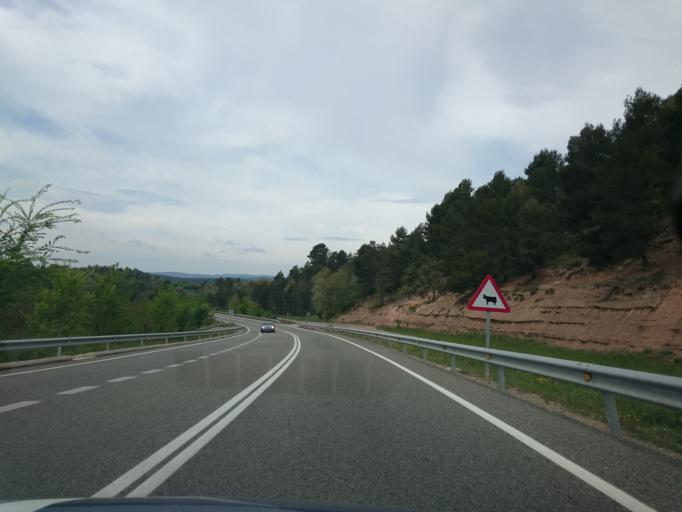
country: ES
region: Catalonia
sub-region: Provincia de Barcelona
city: Olost
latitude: 41.9767
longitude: 2.1140
